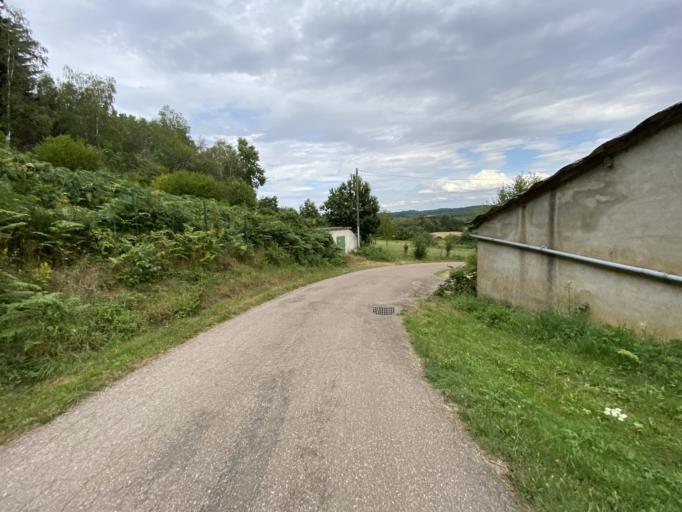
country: FR
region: Bourgogne
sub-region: Departement de la Cote-d'Or
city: Saulieu
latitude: 47.2581
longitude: 4.1330
